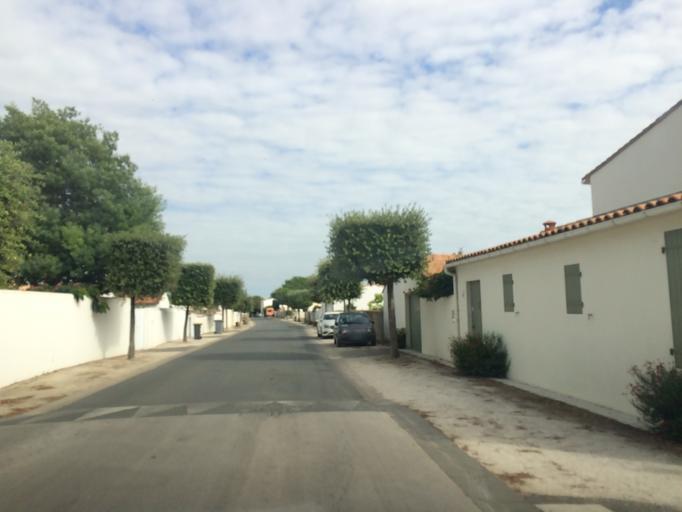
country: FR
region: Poitou-Charentes
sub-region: Departement de la Charente-Maritime
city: La Flotte
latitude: 46.1858
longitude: -1.3325
